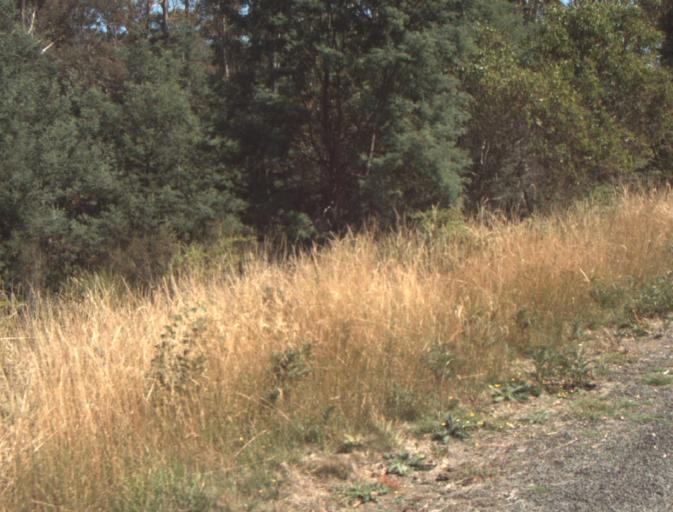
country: AU
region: Tasmania
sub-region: Launceston
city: Newstead
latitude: -41.3580
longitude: 147.3029
